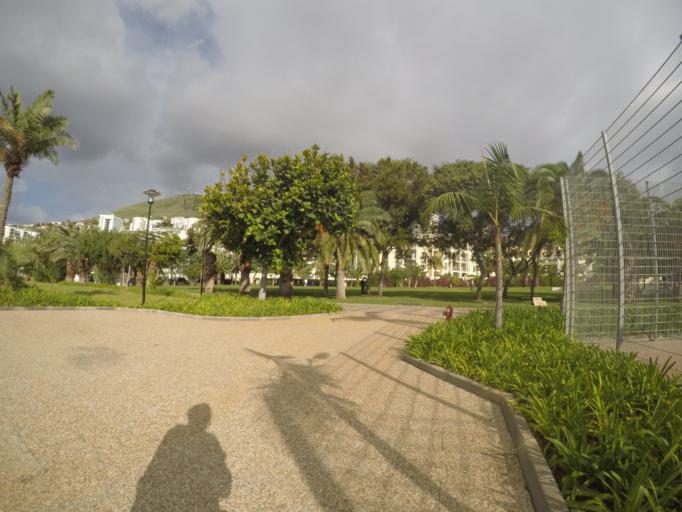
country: PT
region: Madeira
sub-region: Funchal
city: Funchal
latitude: 32.6359
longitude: -16.9331
